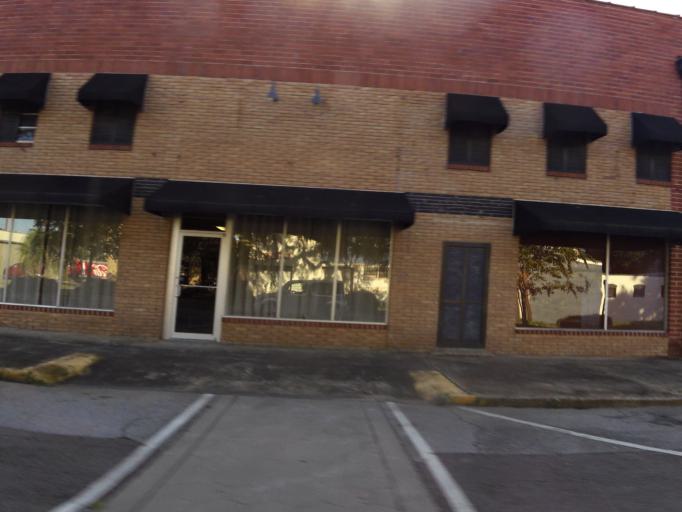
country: US
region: Georgia
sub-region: Glynn County
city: Brunswick
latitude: 31.1455
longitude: -81.4941
